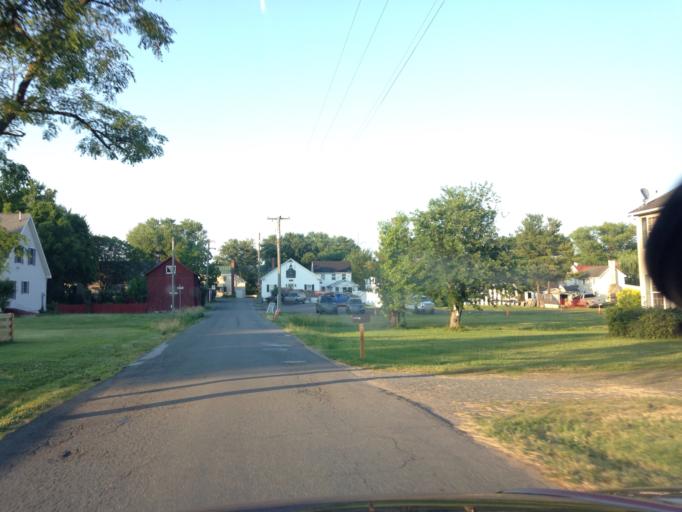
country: US
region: Virginia
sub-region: Loudoun County
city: Lovettsville
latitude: 39.2712
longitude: -77.6371
